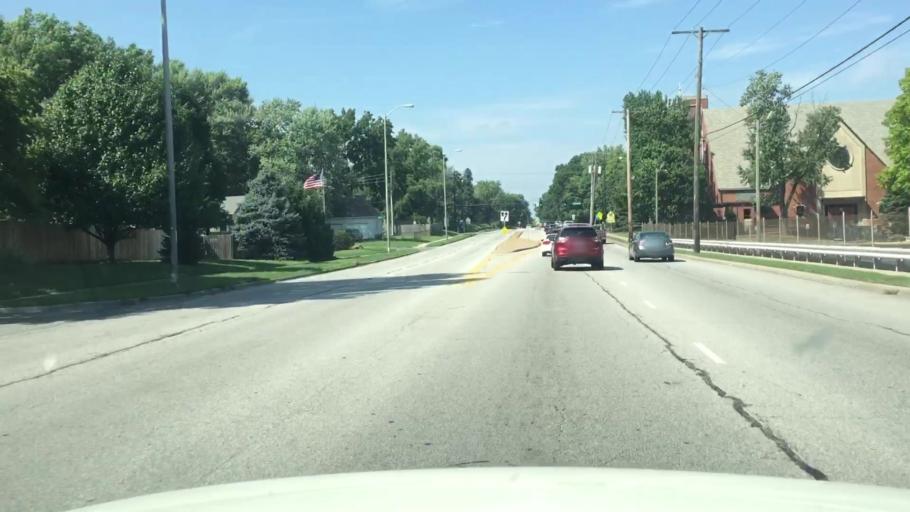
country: US
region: Kansas
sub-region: Johnson County
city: Overland Park
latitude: 38.9987
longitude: -94.6677
